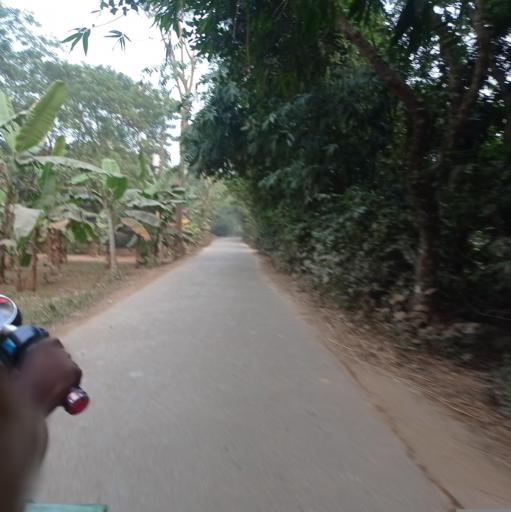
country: BD
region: Dhaka
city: Bajitpur
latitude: 24.1327
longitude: 90.8171
